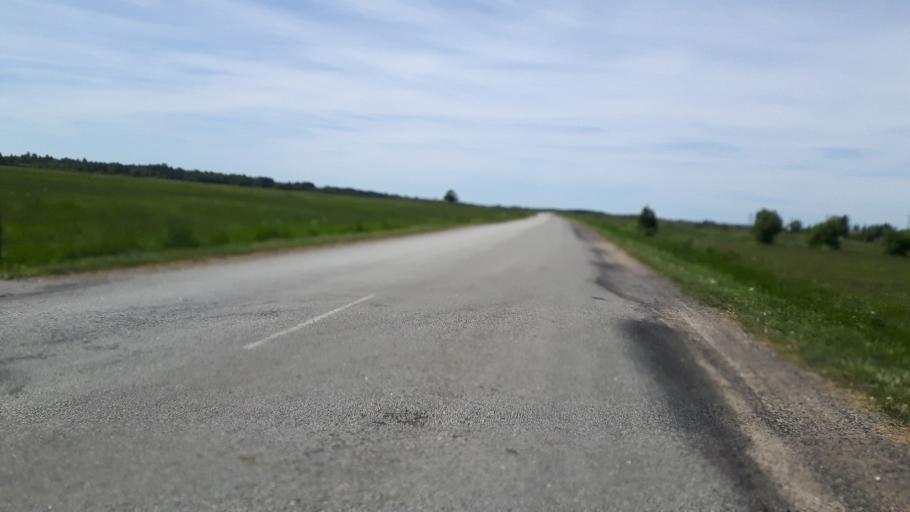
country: EE
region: Harju
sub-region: Kuusalu vald
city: Kuusalu
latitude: 59.4585
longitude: 25.3460
